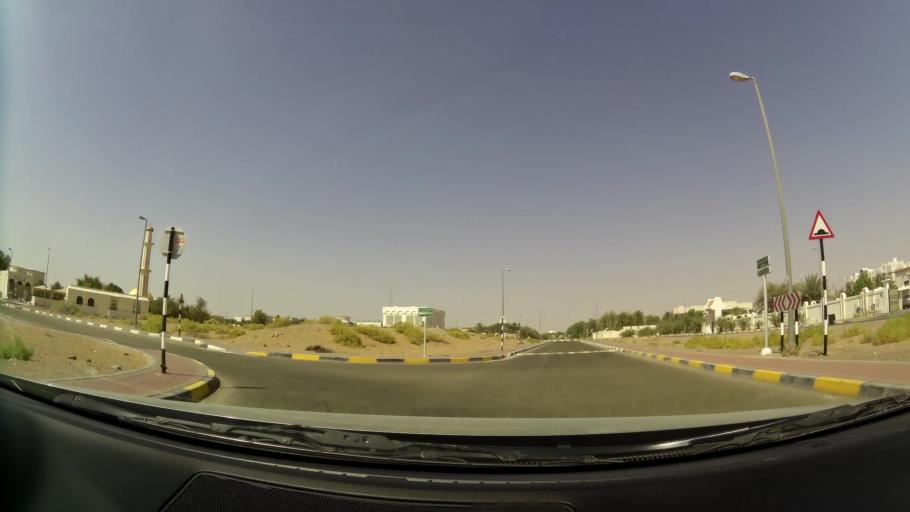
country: OM
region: Al Buraimi
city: Al Buraymi
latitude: 24.3013
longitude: 55.7595
